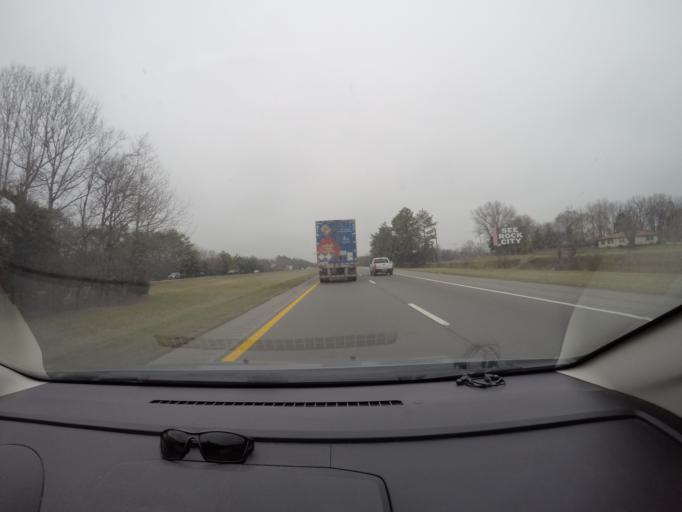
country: US
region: Tennessee
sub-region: Rutherford County
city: Plainview
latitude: 35.7623
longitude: -86.3543
